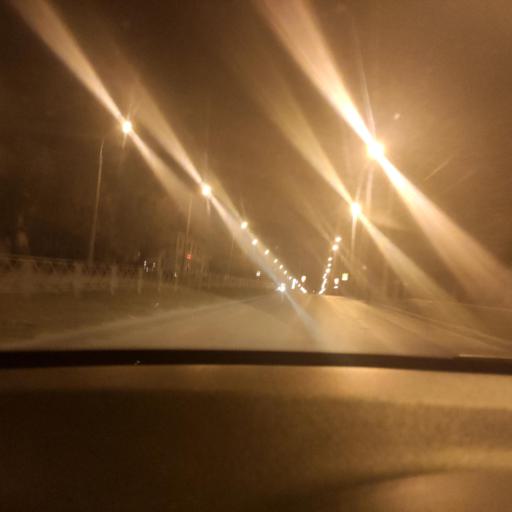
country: RU
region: Samara
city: Samara
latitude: 53.2019
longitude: 50.2141
